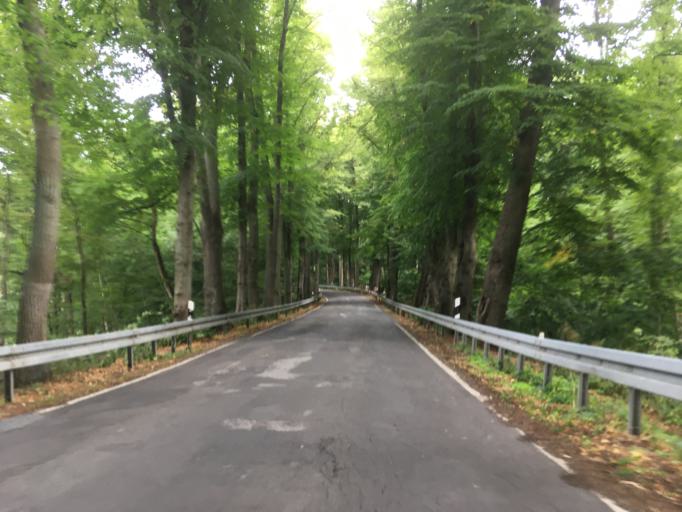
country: DE
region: Brandenburg
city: Mittenwalde
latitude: 53.2440
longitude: 13.5937
